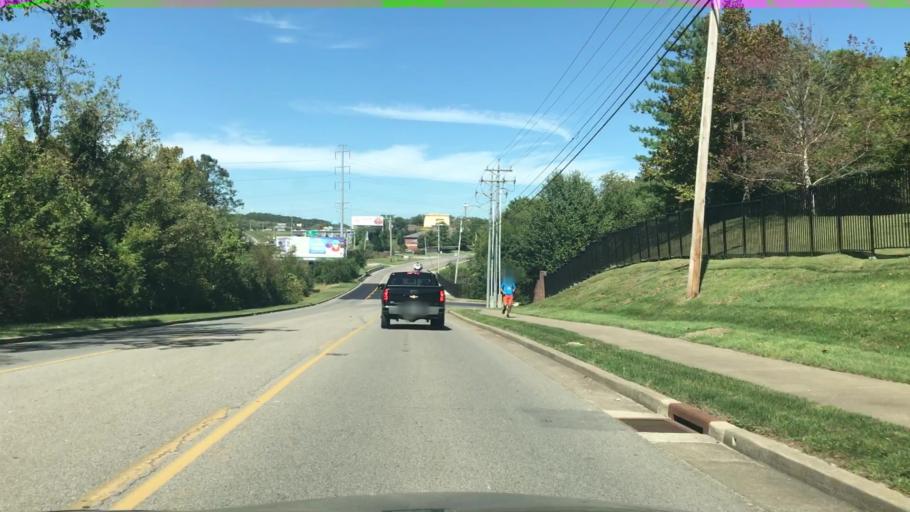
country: US
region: Tennessee
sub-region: Williamson County
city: Franklin
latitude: 35.9060
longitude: -86.8245
